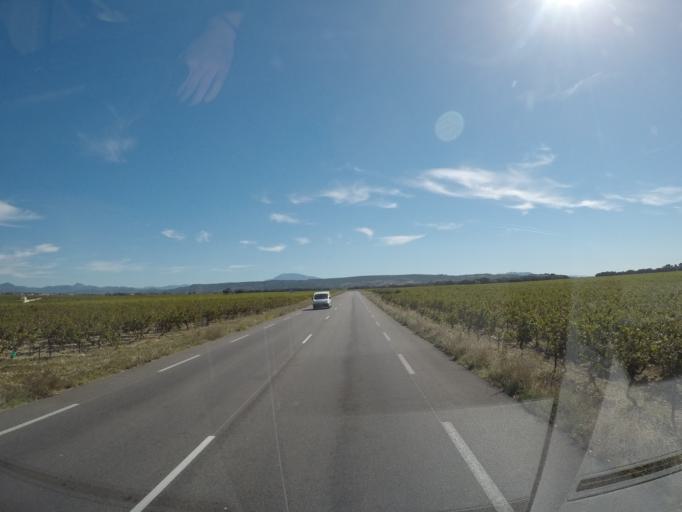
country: FR
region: Rhone-Alpes
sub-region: Departement de la Drome
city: Tulette
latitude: 44.2802
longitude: 4.8941
